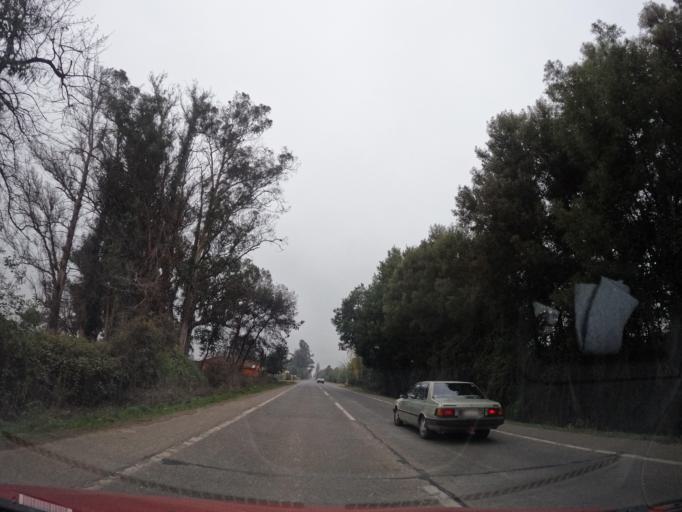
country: CL
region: Maule
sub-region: Provincia de Talca
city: San Clemente
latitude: -35.5647
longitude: -71.4499
